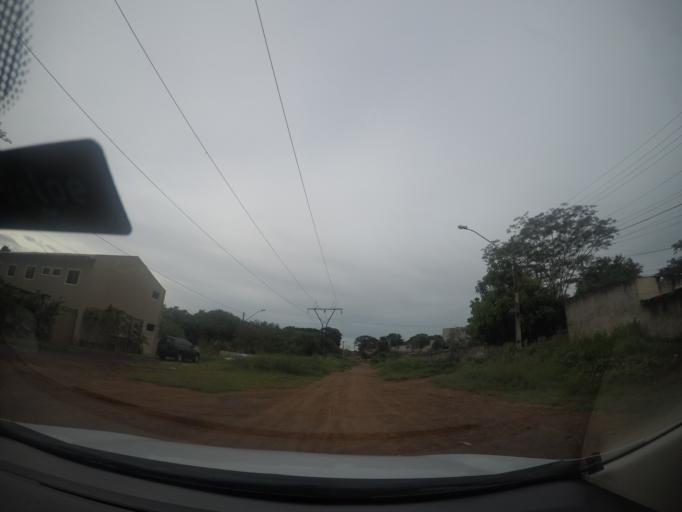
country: BR
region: Goias
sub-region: Goiania
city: Goiania
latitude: -16.6346
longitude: -49.2421
